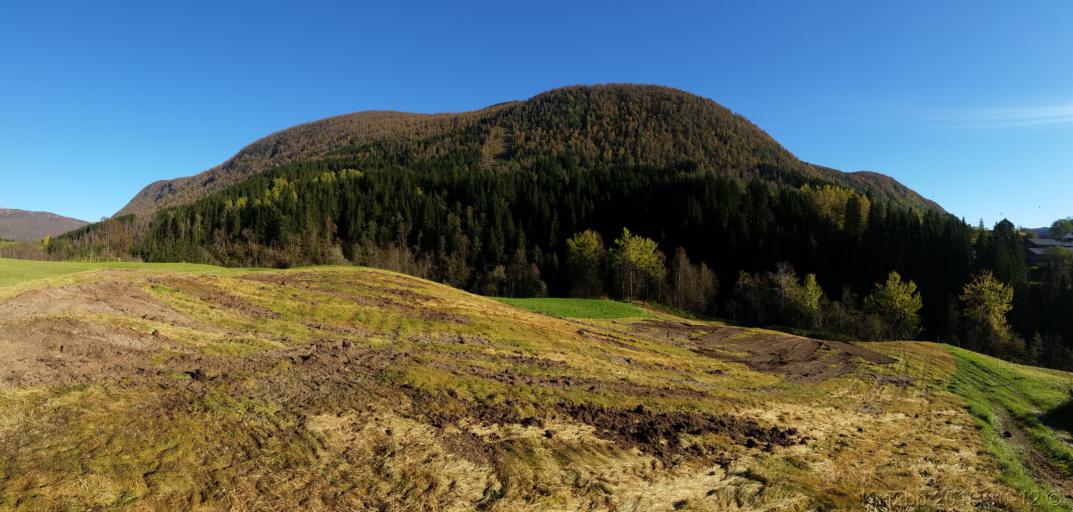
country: NO
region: Hordaland
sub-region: Voss
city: Voss
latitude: 60.8353
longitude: 6.4631
